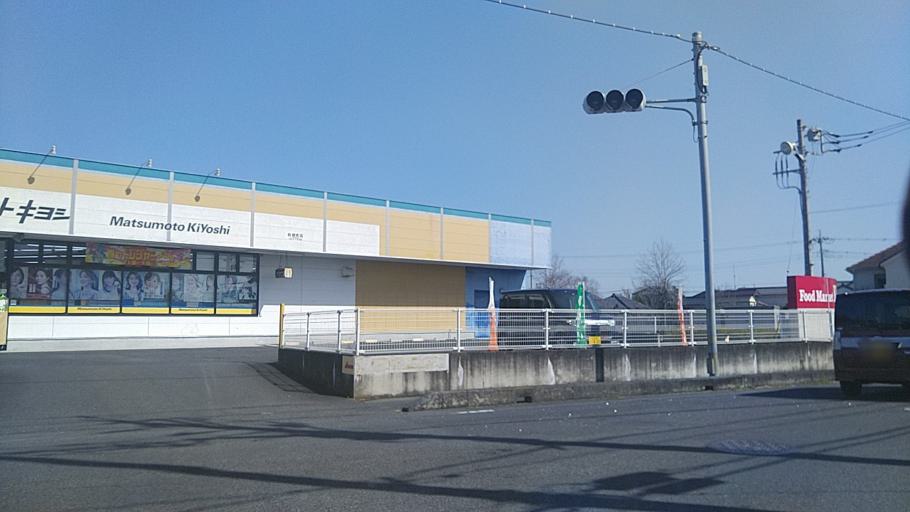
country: JP
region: Ibaraki
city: Ryugasaki
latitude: 35.8551
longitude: 140.1500
